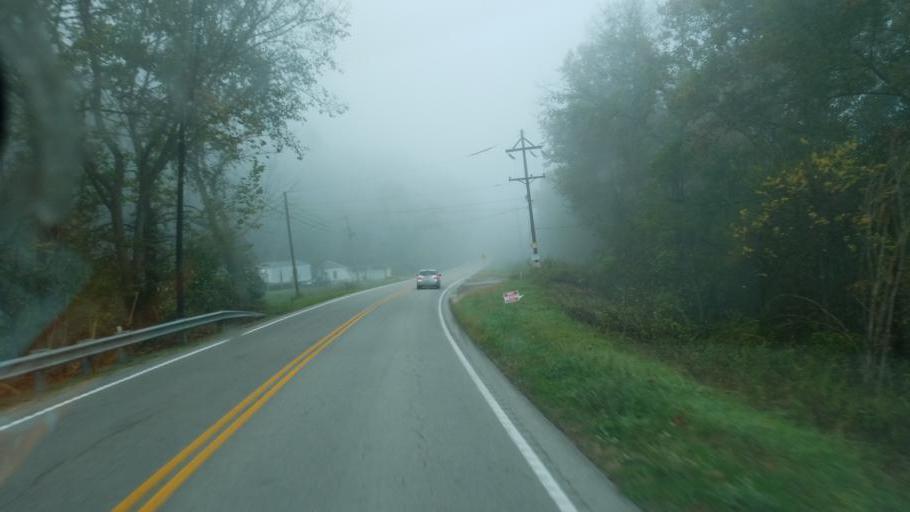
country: US
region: Ohio
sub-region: Scioto County
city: Portsmouth
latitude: 38.6900
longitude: -83.0527
